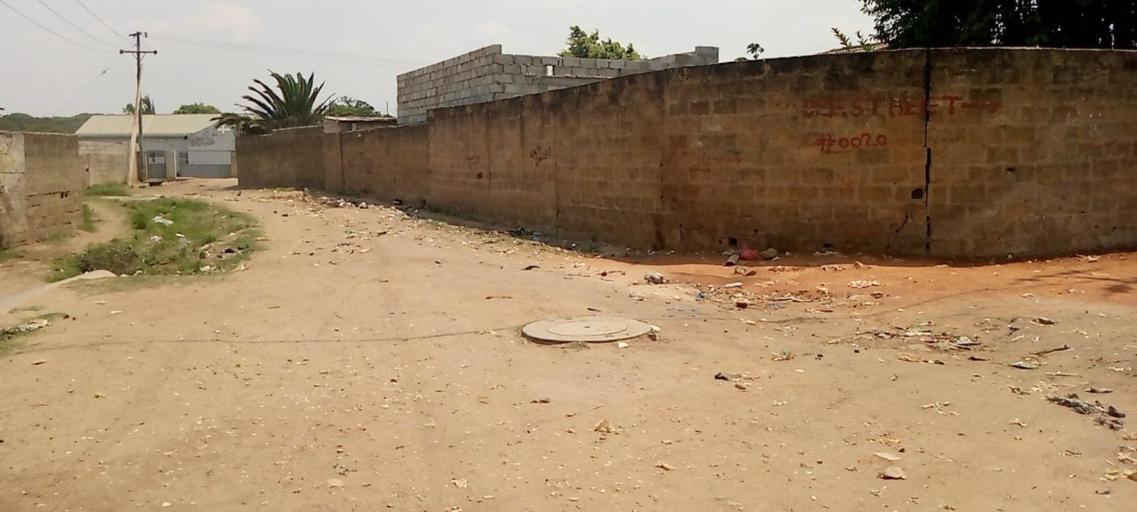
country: ZM
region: Lusaka
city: Lusaka
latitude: -15.3999
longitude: 28.3460
